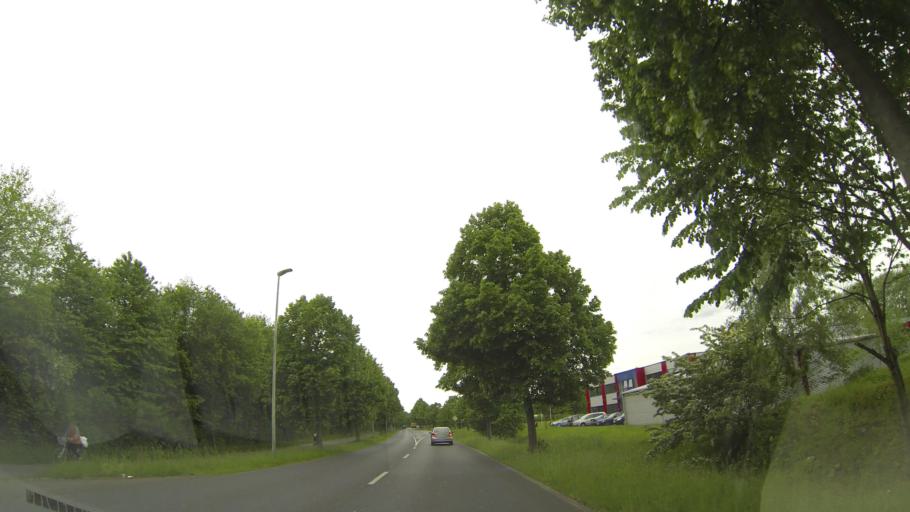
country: DE
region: Schleswig-Holstein
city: Halstenbek
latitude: 53.6265
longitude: 9.8682
